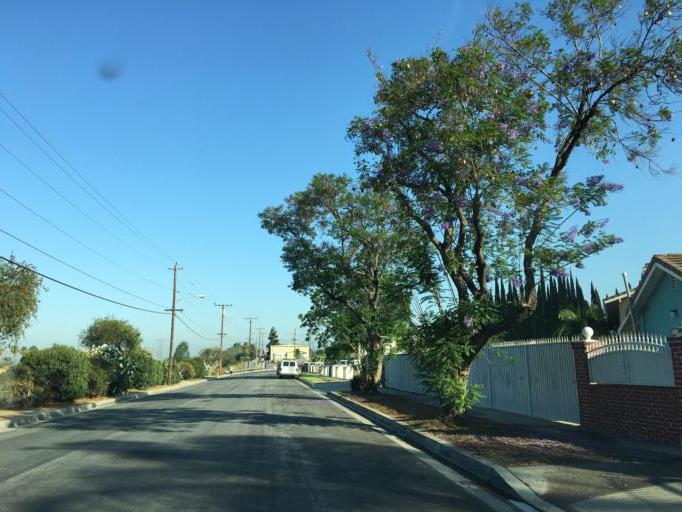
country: US
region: California
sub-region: Los Angeles County
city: Avocado Heights
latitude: 34.0342
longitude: -118.0173
